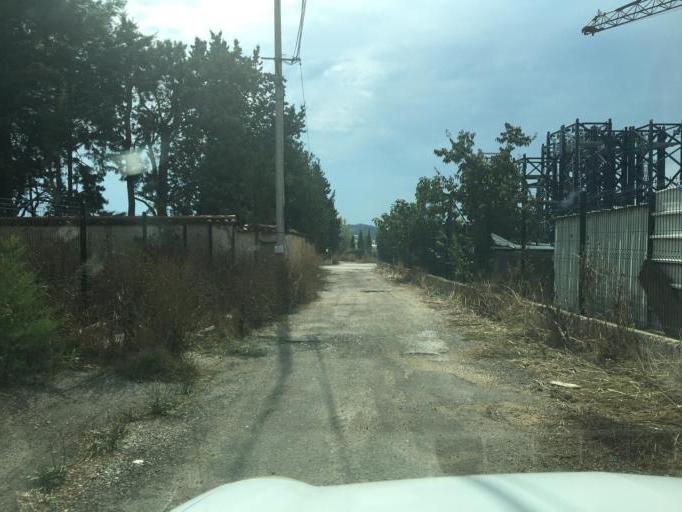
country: FR
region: Provence-Alpes-Cote d'Azur
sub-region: Departement des Bouches-du-Rhone
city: Bouc-Bel-Air
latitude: 43.4852
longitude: 5.3914
